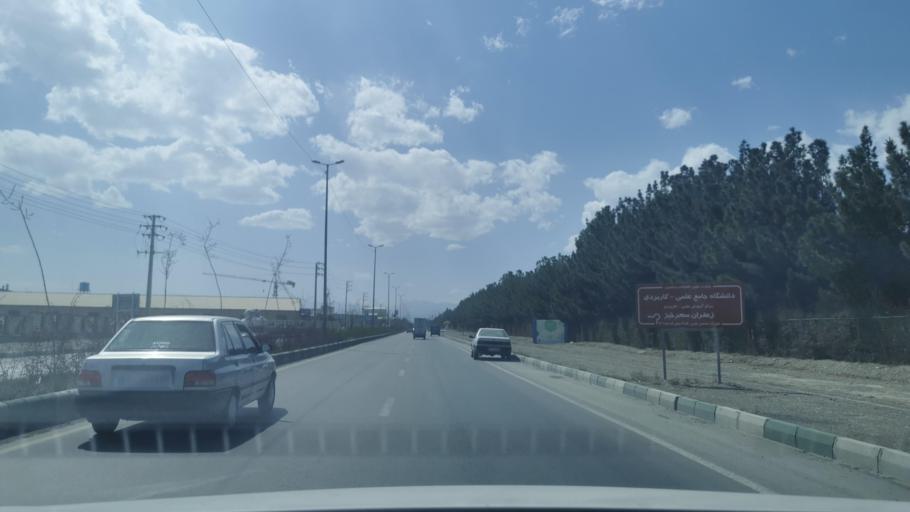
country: IR
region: Razavi Khorasan
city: Torqabeh
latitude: 36.4320
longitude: 59.4247
